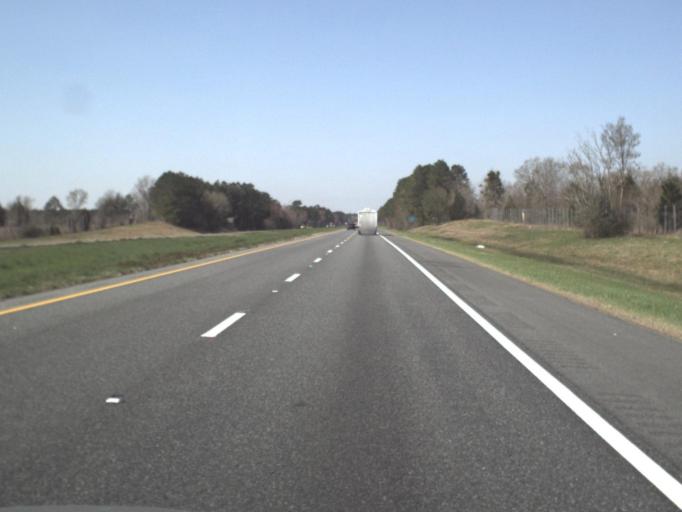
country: US
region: Florida
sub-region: Washington County
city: Chipley
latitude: 30.7470
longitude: -85.4291
